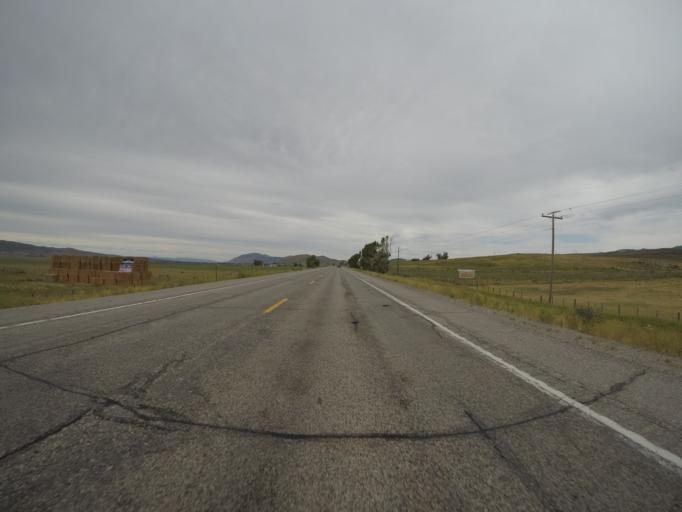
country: US
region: Utah
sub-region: Rich County
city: Randolph
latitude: 42.0411
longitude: -110.9315
